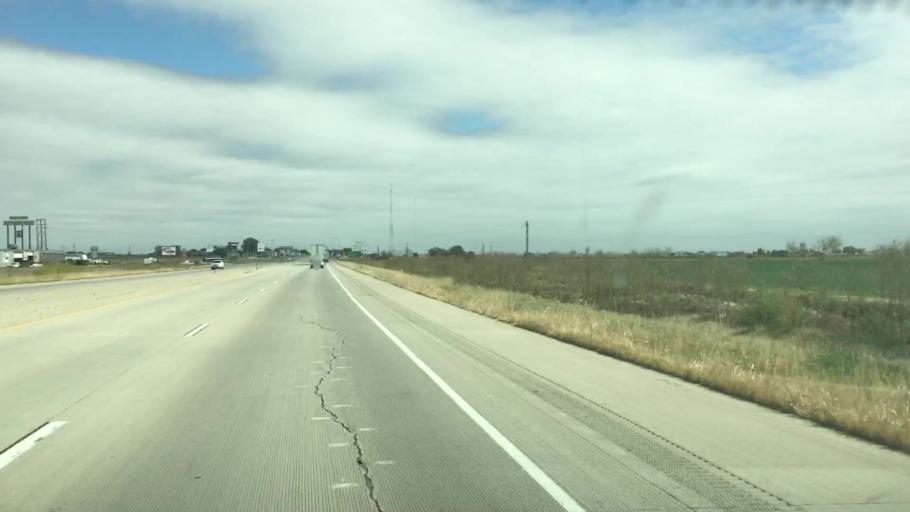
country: US
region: Colorado
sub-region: Prowers County
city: Lamar
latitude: 38.1132
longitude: -102.6365
